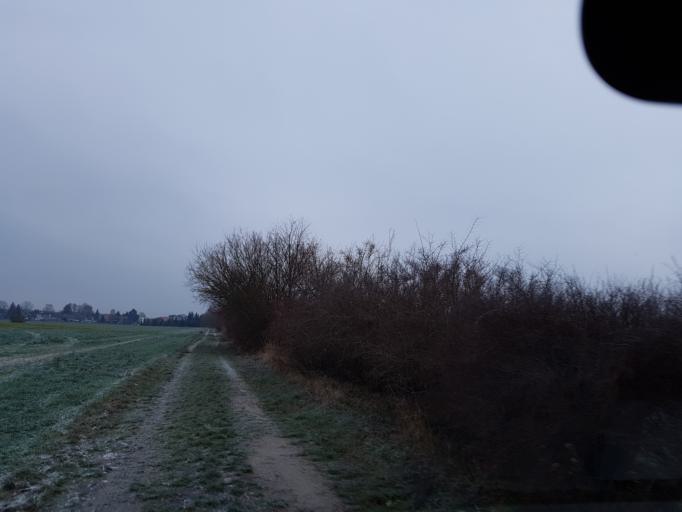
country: DE
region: Brandenburg
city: Ruckersdorf
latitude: 51.5693
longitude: 13.5489
